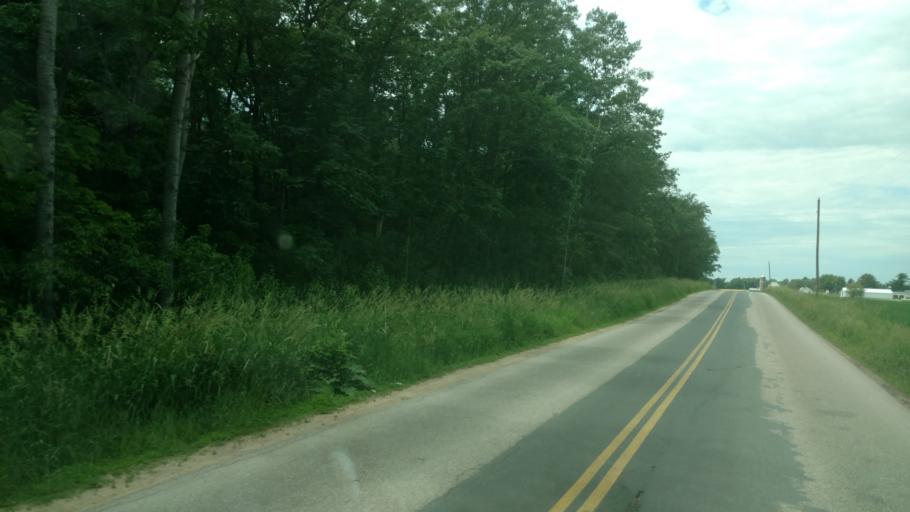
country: US
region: Wisconsin
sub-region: Juneau County
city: Elroy
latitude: 43.8095
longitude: -90.4352
